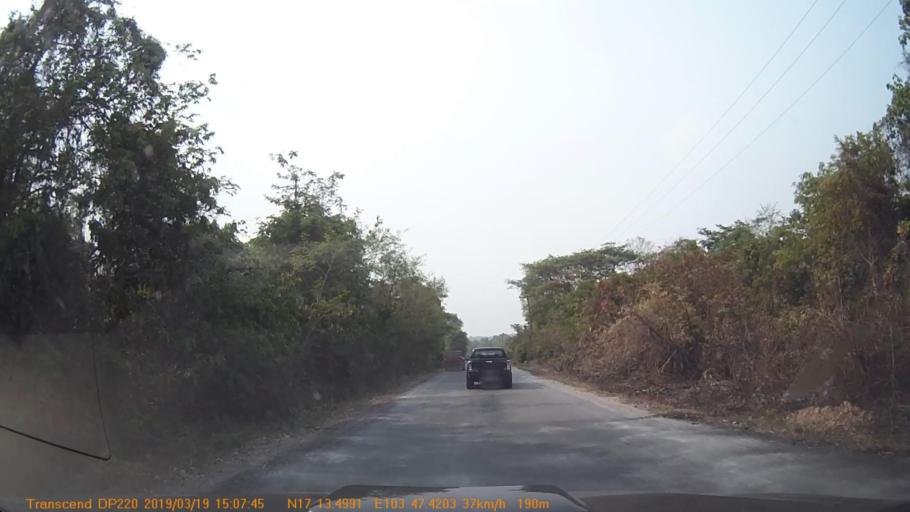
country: TH
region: Sakon Nakhon
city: Nikhom Nam Un
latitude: 17.2251
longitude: 103.7903
